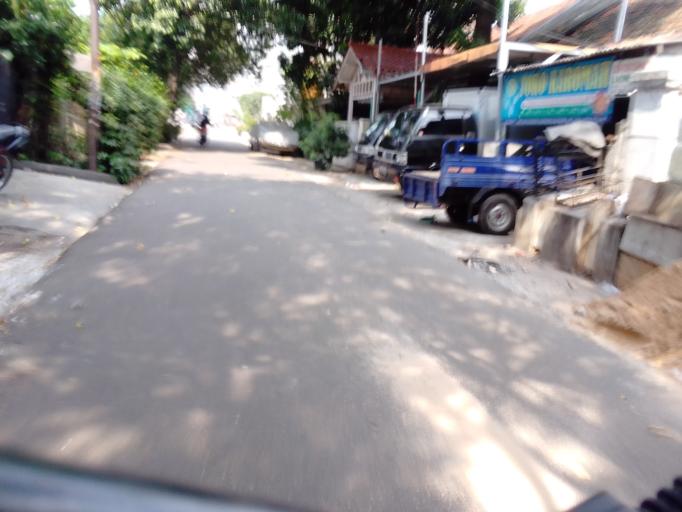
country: ID
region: Jakarta Raya
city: Jakarta
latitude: -6.2084
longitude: 106.8102
